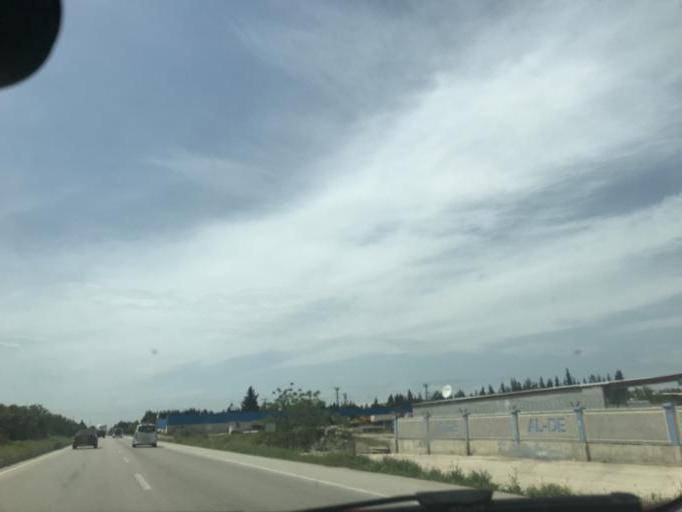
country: TR
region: Adana
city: Yakapinar
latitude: 36.9708
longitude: 35.5261
